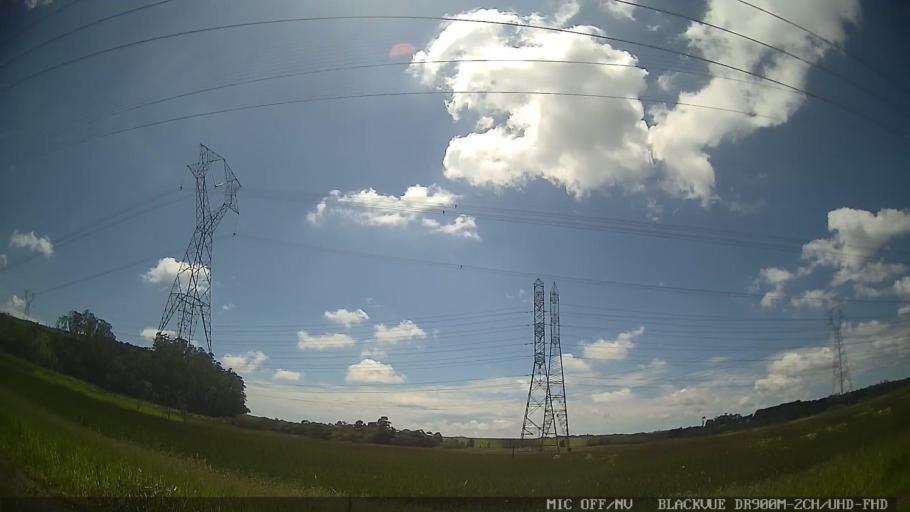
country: BR
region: Sao Paulo
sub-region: Mogi das Cruzes
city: Mogi das Cruzes
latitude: -23.6249
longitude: -46.2037
